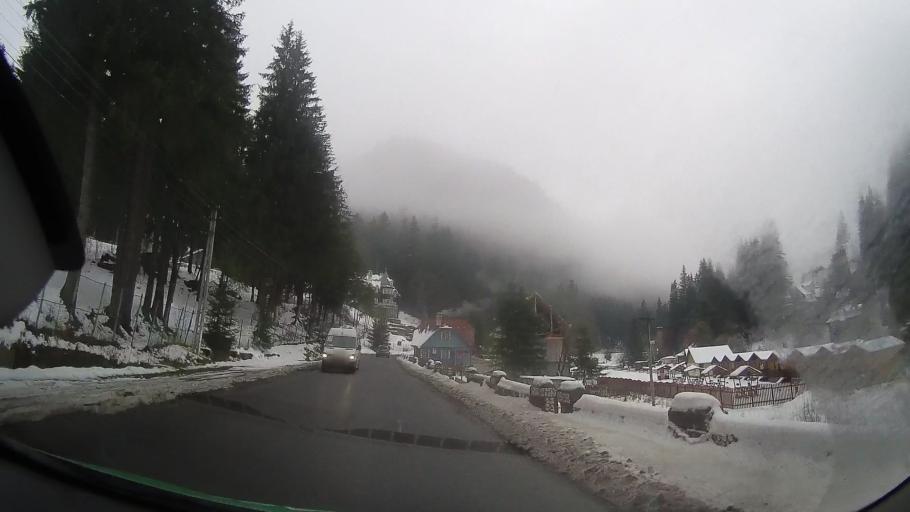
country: RO
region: Neamt
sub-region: Comuna Bicaz Chei
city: Bicaz Chei
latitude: 46.7962
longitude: 25.8014
